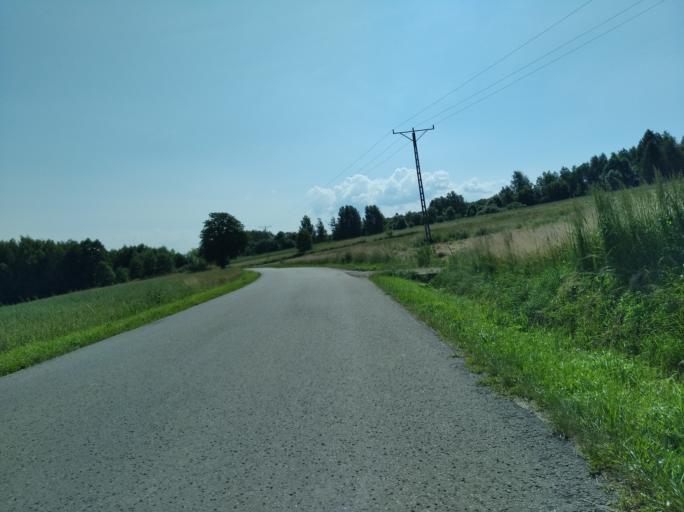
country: PL
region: Subcarpathian Voivodeship
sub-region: Powiat rzeszowski
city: Dynow
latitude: 49.8129
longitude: 22.2095
